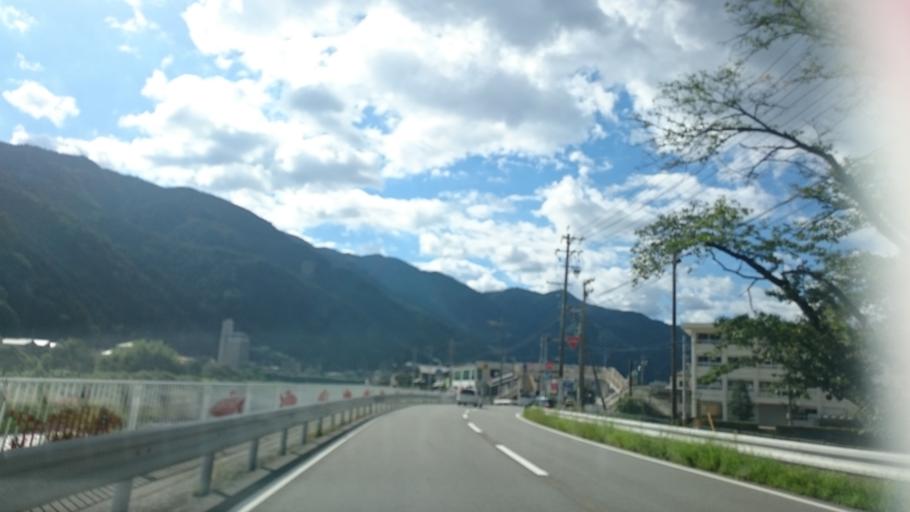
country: JP
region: Gifu
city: Gujo
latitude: 35.7987
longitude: 137.2524
